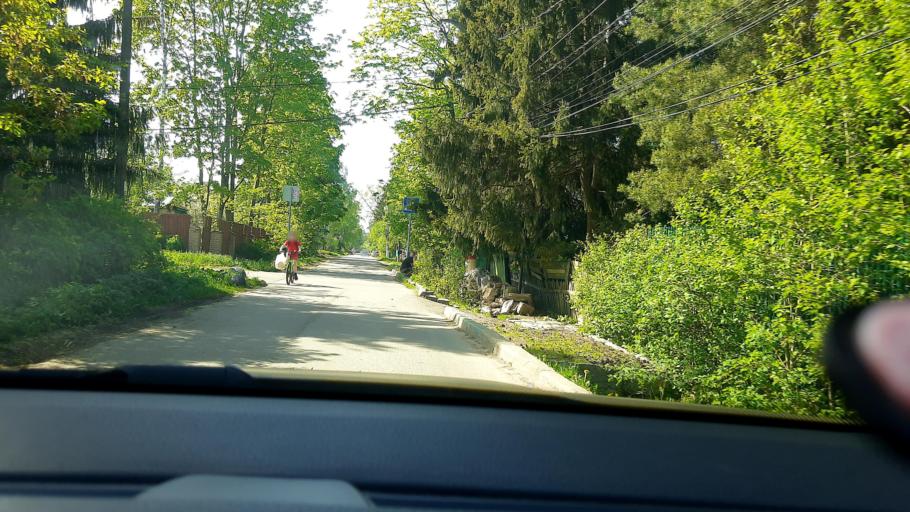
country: RU
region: Moskovskaya
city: Skhodnya
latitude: 55.9443
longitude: 37.3169
